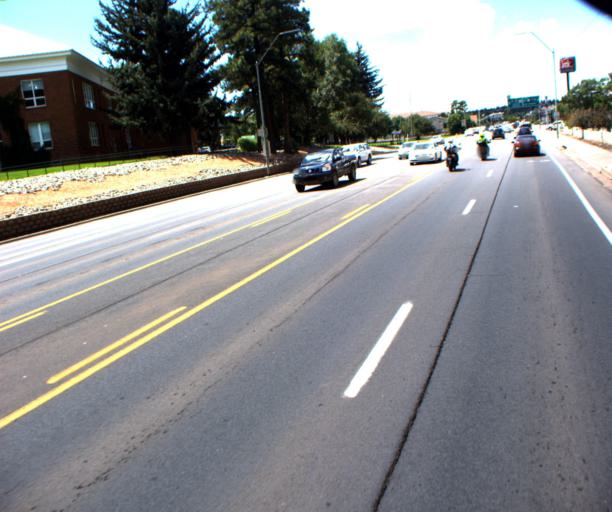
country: US
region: Arizona
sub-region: Coconino County
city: Flagstaff
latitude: 35.1946
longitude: -111.6562
